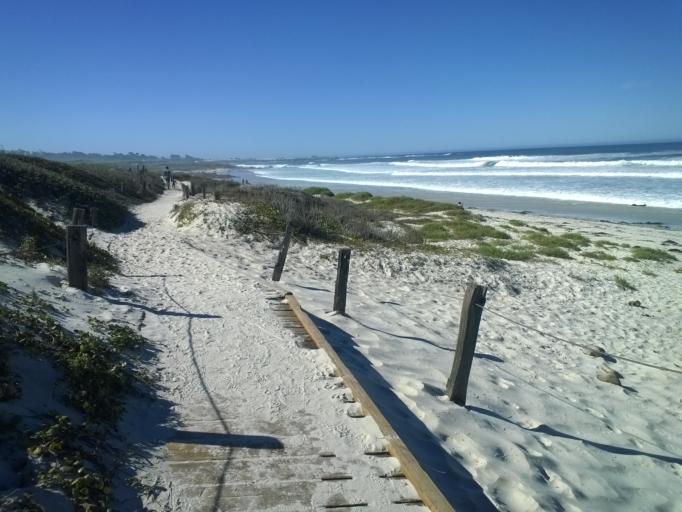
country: US
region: California
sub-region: Monterey County
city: Pacific Grove
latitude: 36.6169
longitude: -121.9419
